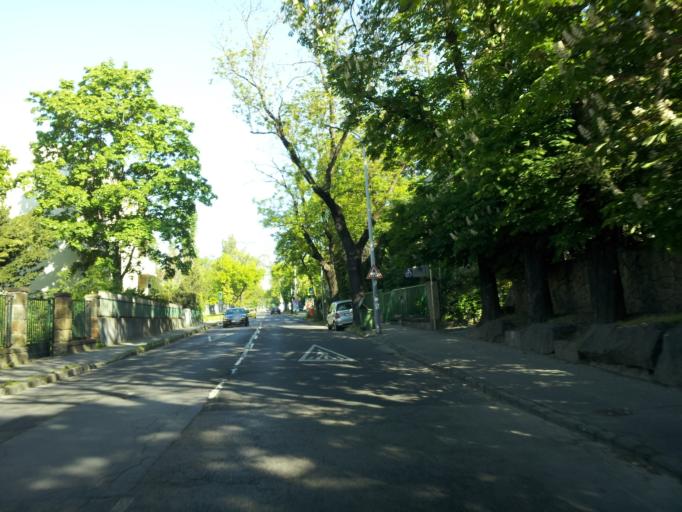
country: HU
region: Budapest
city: Budapest XII. keruelet
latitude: 47.5197
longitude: 19.0004
